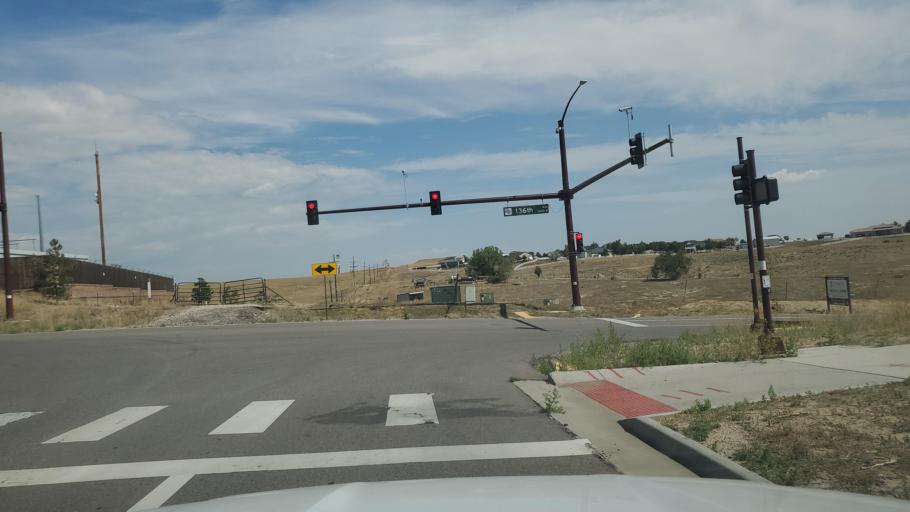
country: US
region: Colorado
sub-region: Adams County
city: Todd Creek
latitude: 39.9428
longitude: -104.8844
